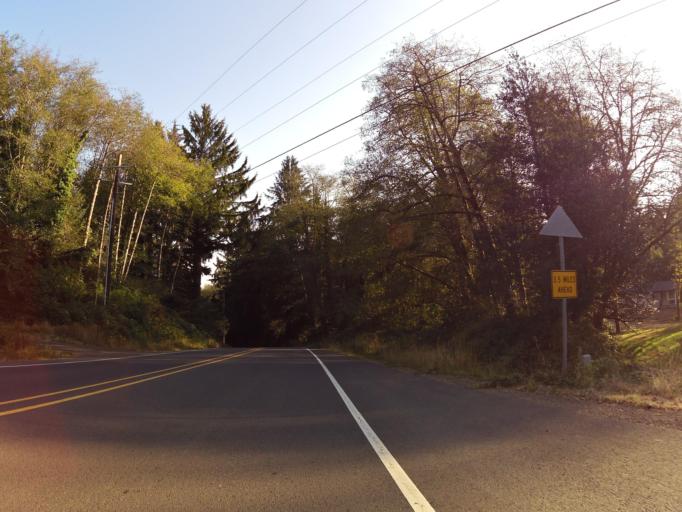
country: US
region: Oregon
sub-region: Lincoln County
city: Lincoln City
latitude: 45.0054
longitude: -123.9802
